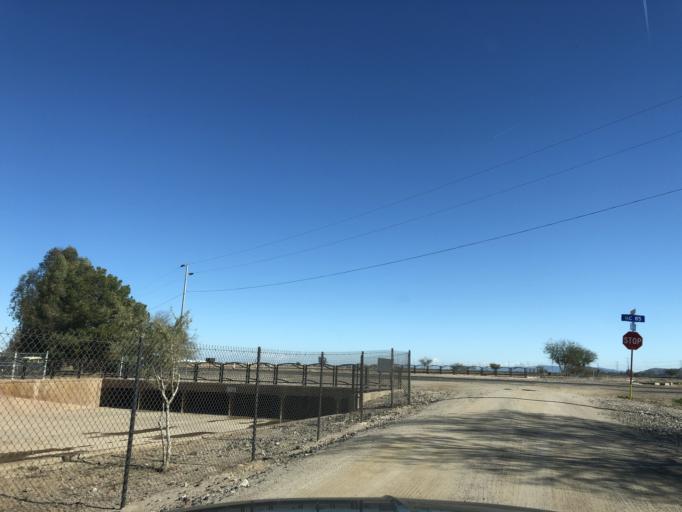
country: US
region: Arizona
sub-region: Maricopa County
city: Goodyear
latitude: 33.4002
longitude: -112.4392
